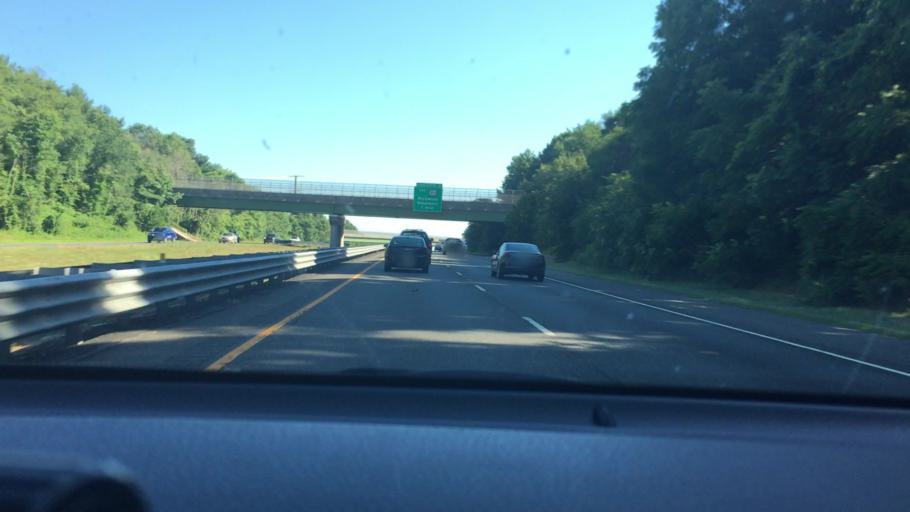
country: US
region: New Jersey
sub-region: Gloucester County
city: Pitman
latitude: 39.7354
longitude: -75.1500
